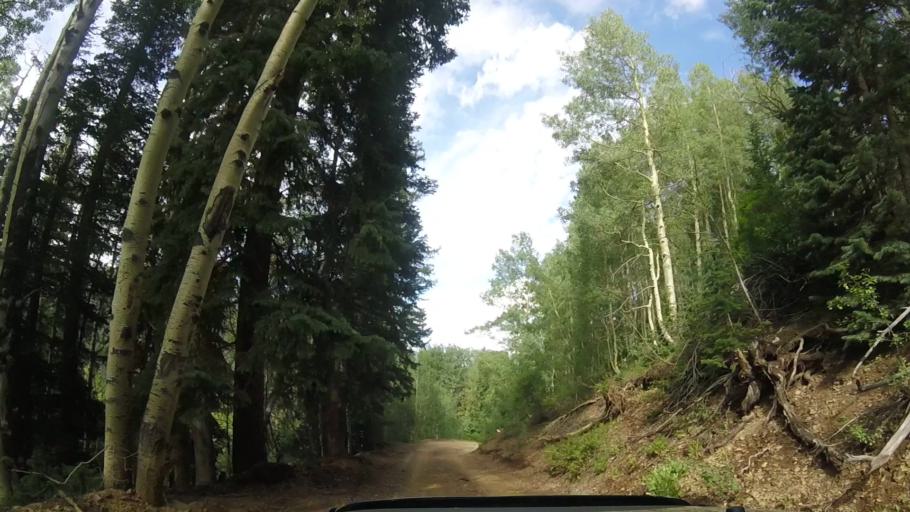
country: US
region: Colorado
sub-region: San Miguel County
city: Telluride
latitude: 37.8598
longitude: -107.7961
